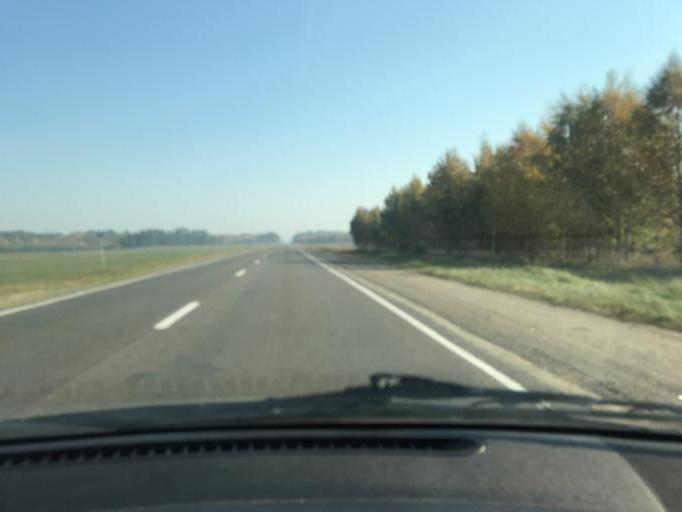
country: BY
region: Brest
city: Horad Luninyets
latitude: 52.3036
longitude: 26.4859
